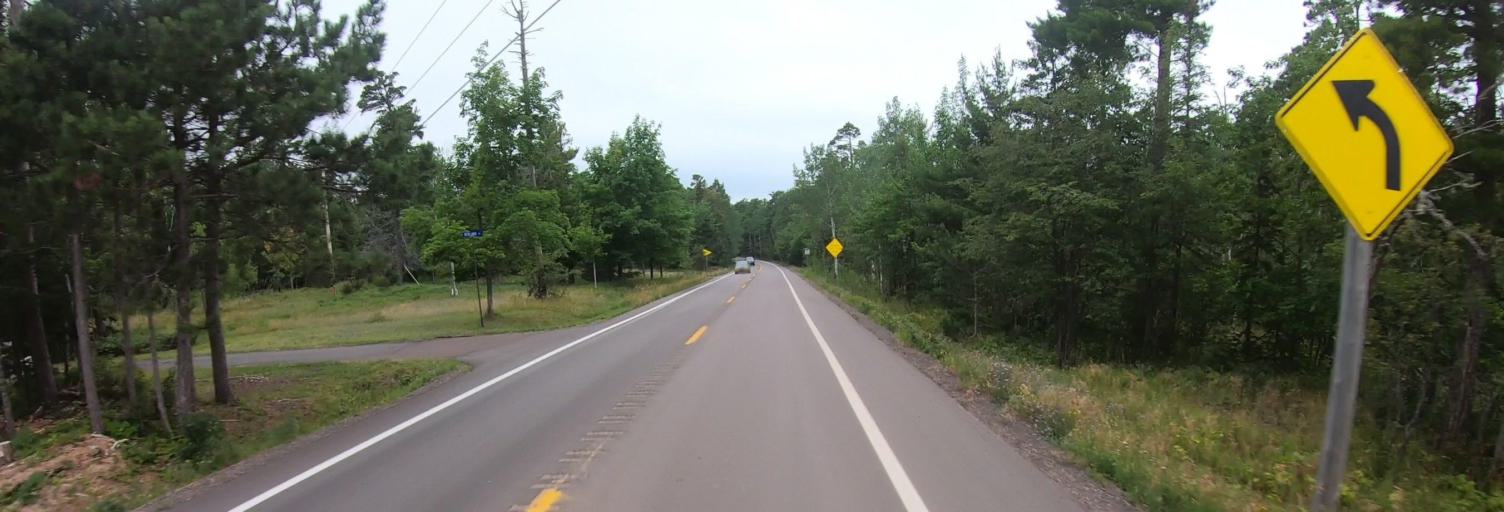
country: US
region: Michigan
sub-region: Keweenaw County
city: Eagle River
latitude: 47.4668
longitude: -87.8550
